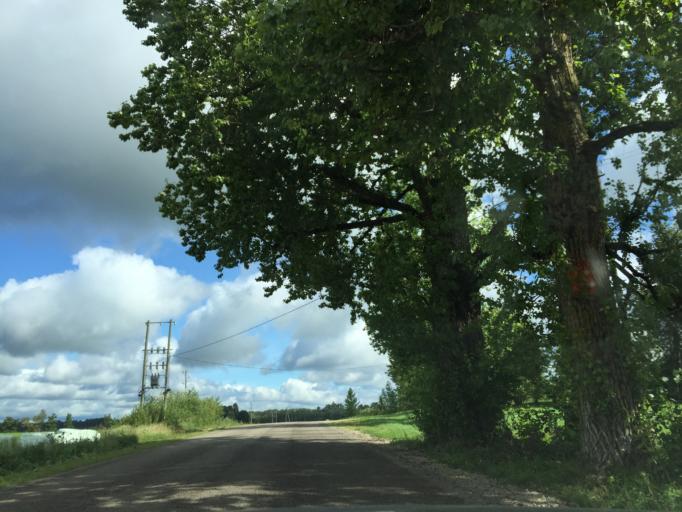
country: LV
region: Sigulda
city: Sigulda
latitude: 57.1779
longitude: 24.9252
